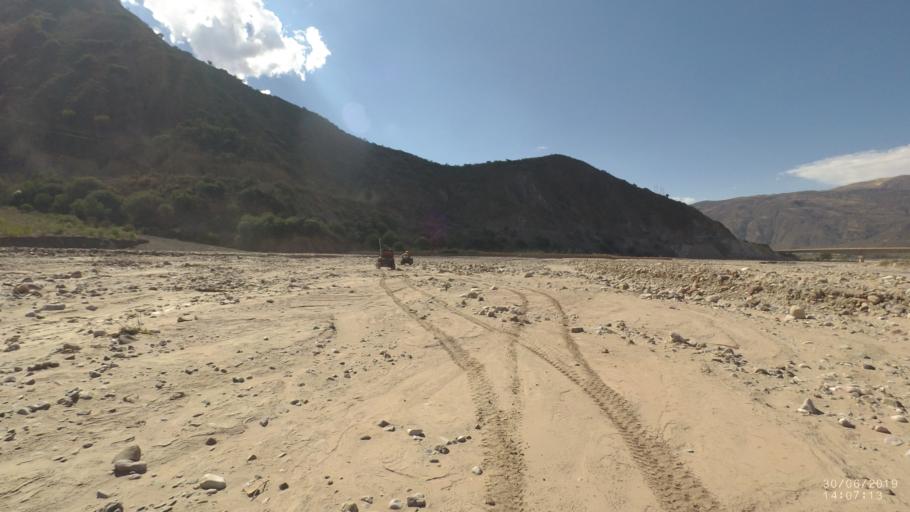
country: BO
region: Cochabamba
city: Irpa Irpa
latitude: -17.8018
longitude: -66.3545
